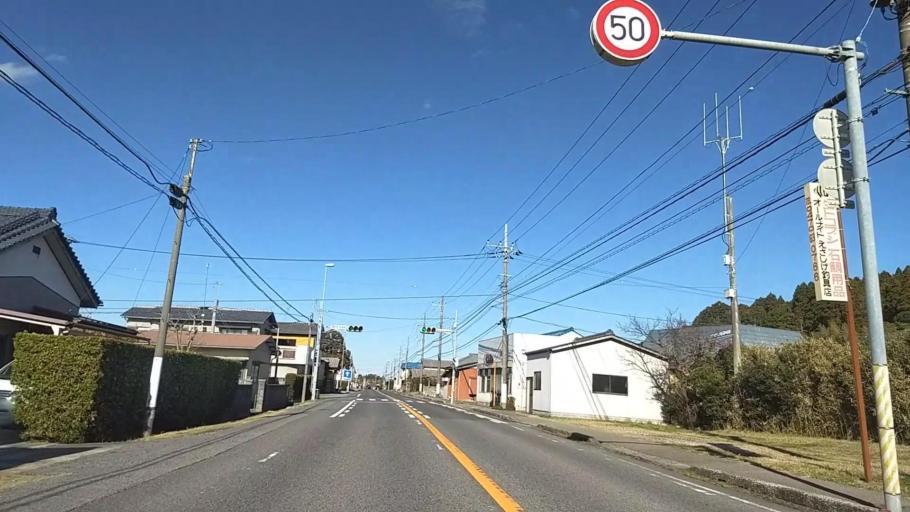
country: JP
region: Chiba
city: Ohara
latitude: 35.2295
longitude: 140.3876
